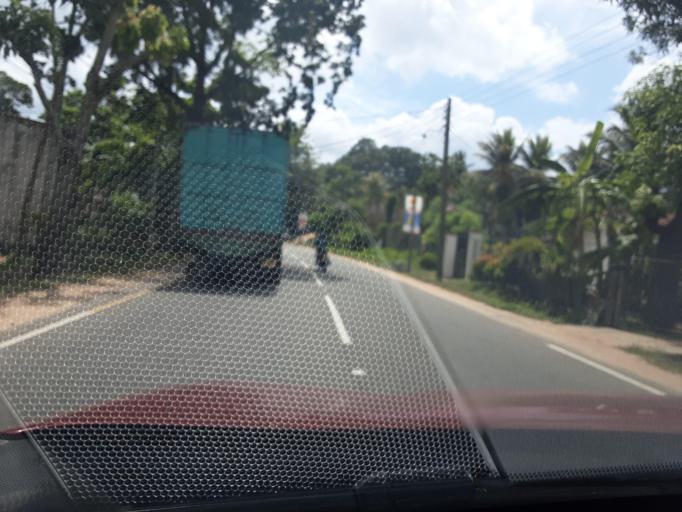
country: LK
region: North Western
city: Kuliyapitiya
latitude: 7.4504
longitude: 80.1949
